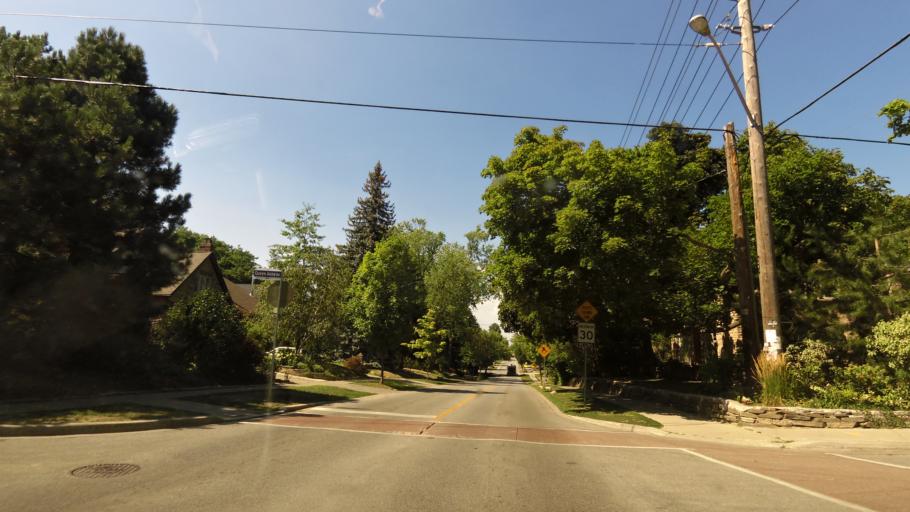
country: CA
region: Ontario
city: Etobicoke
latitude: 43.6561
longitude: -79.5086
